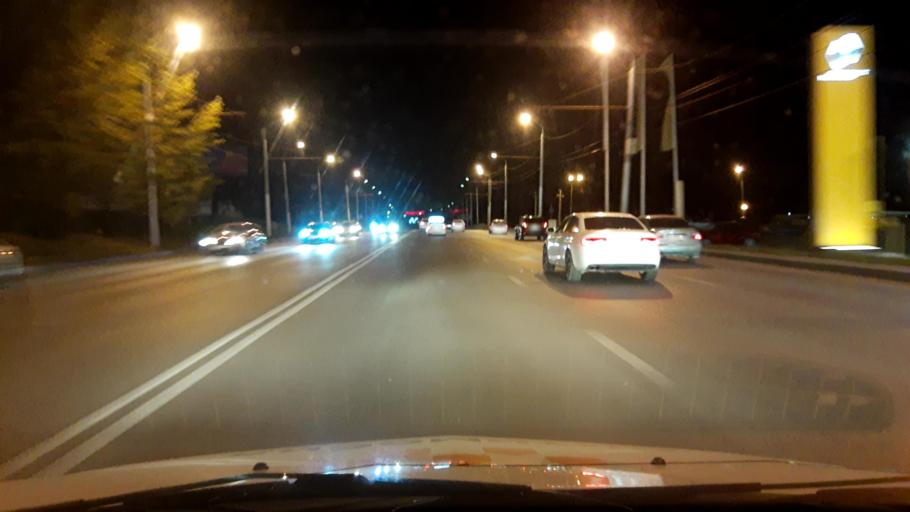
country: RU
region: Bashkortostan
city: Ufa
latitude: 54.7840
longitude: 56.0749
